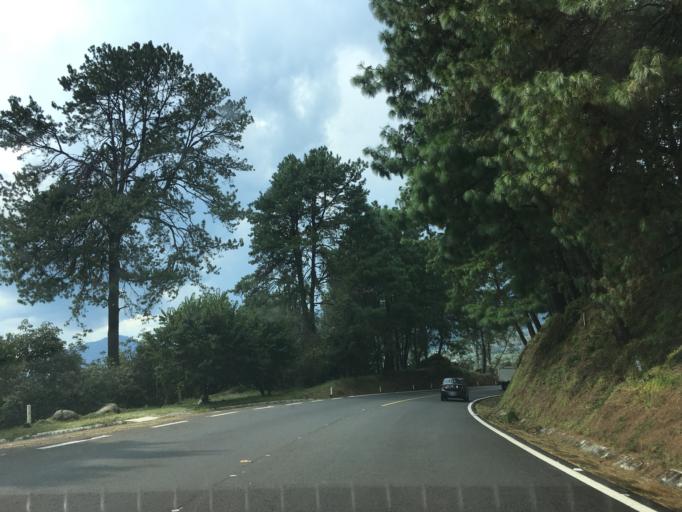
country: MX
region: Michoacan
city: Tingambato
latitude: 19.4957
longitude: -101.8375
